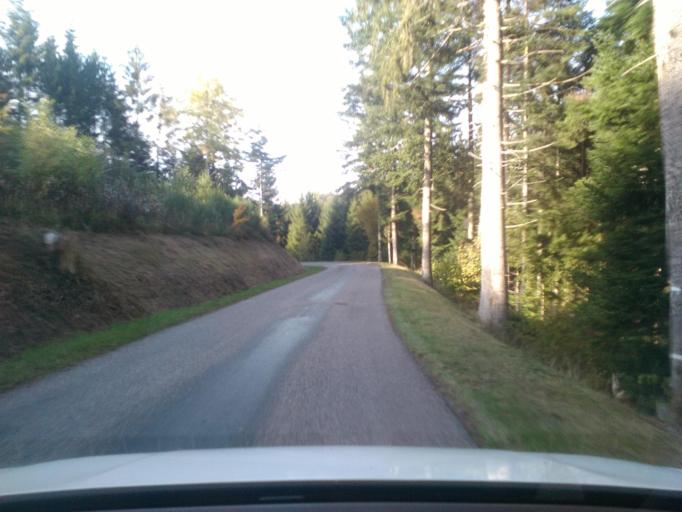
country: FR
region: Lorraine
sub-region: Departement des Vosges
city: Sainte-Marguerite
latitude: 48.3211
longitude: 7.0322
